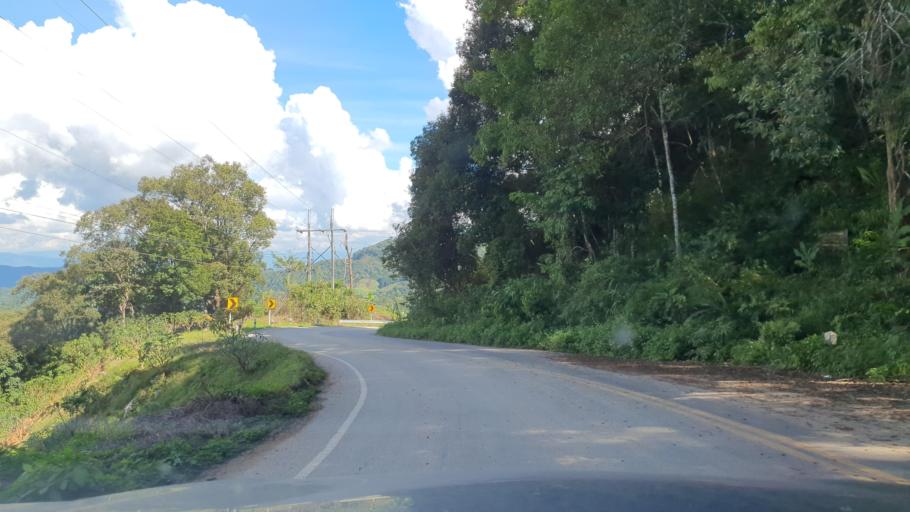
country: TH
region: Chiang Mai
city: Phrao
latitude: 19.3108
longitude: 99.3368
